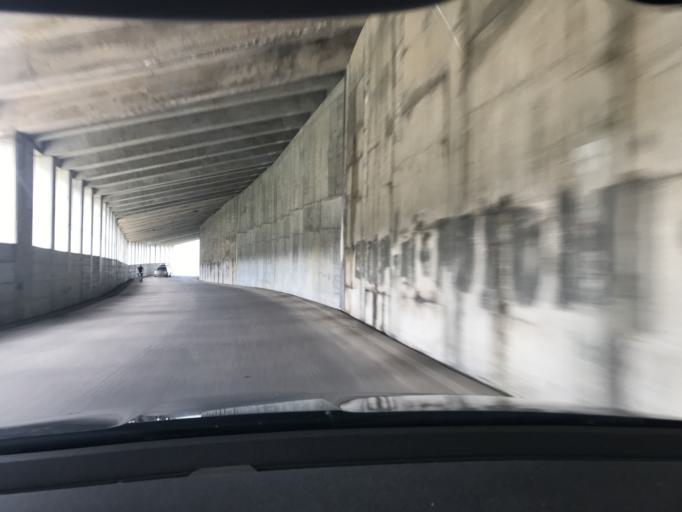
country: IT
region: Veneto
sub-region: Provincia di Belluno
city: Livinallongo del Col di Lana
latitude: 46.5183
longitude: 12.0032
